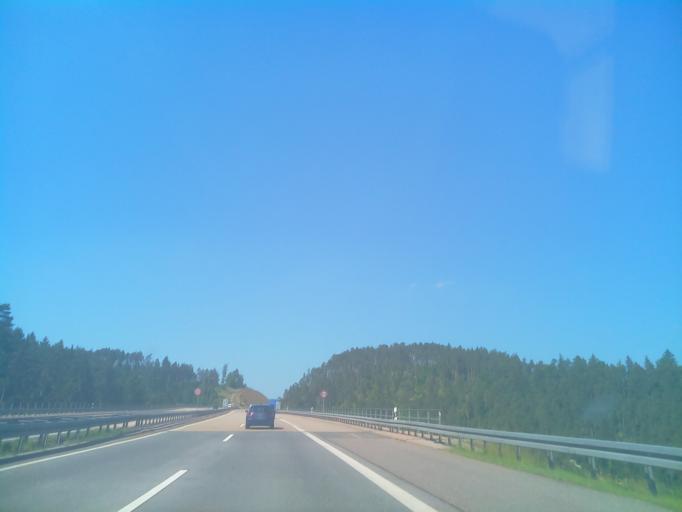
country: DE
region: Thuringia
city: Ellingshausen
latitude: 50.5683
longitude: 10.4803
